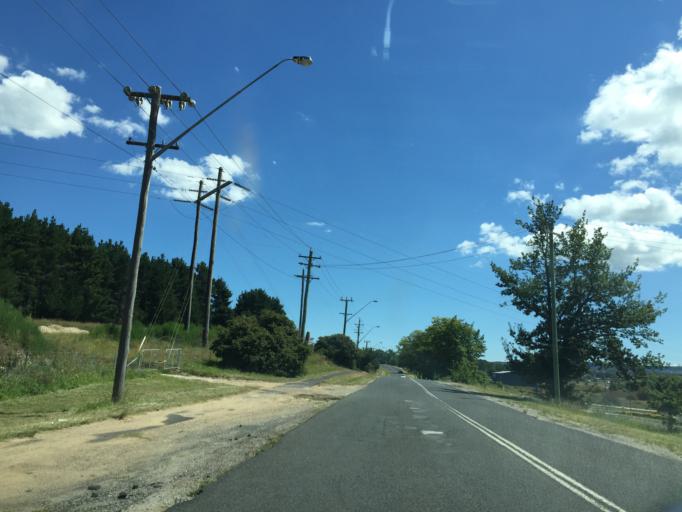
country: AU
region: New South Wales
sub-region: Lithgow
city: Lithgow
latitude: -33.4037
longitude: 150.0724
